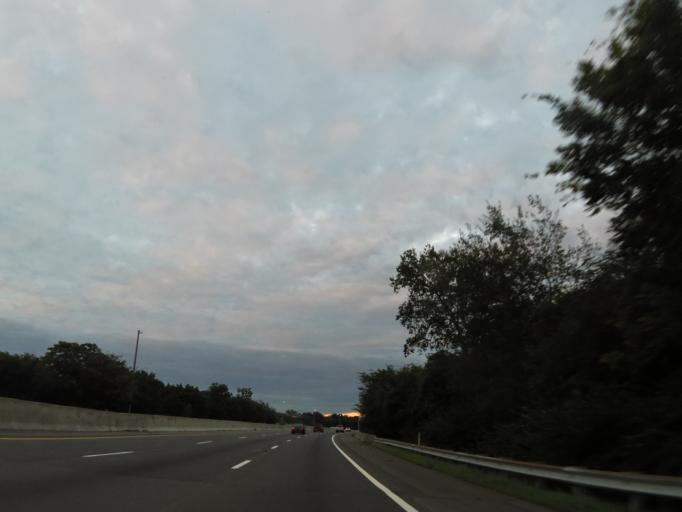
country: US
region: Tennessee
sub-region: Davidson County
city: Belle Meade
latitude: 36.1484
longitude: -86.8757
